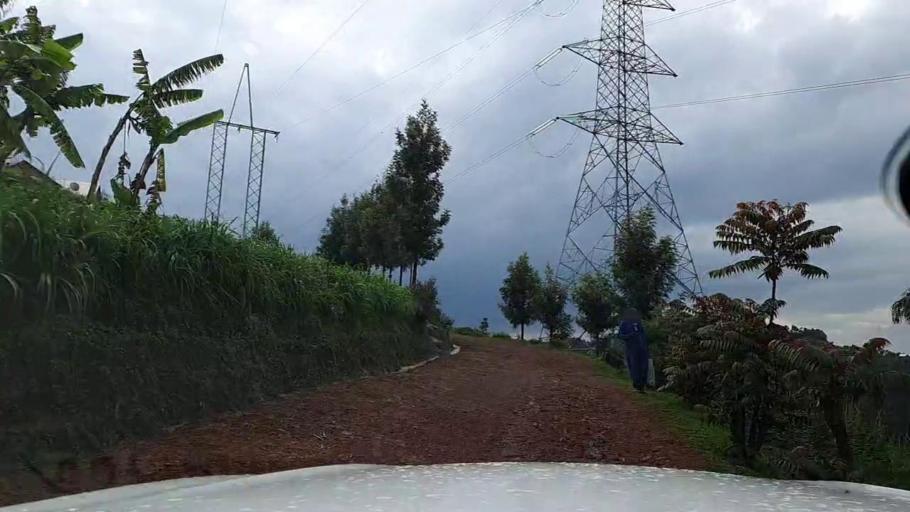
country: RW
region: Northern Province
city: Byumba
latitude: -1.7197
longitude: 29.9075
